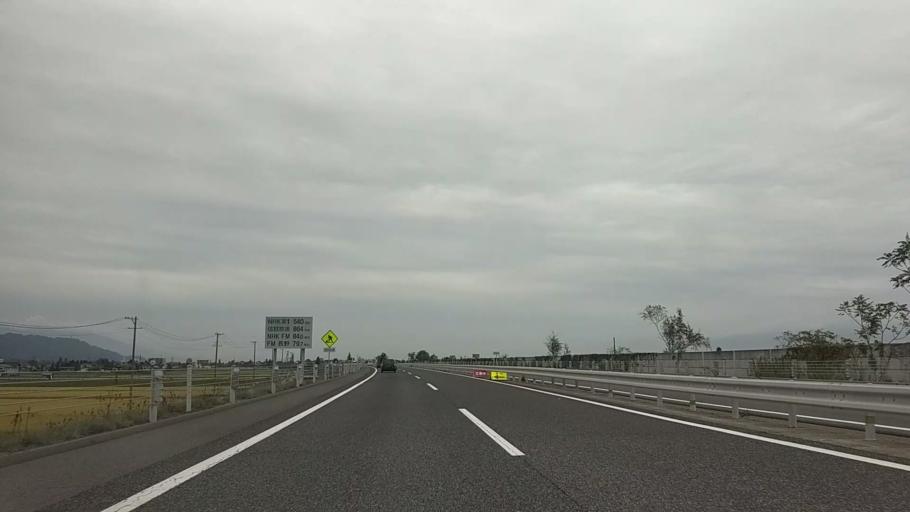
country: JP
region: Nagano
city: Toyoshina
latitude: 36.3142
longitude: 137.9205
